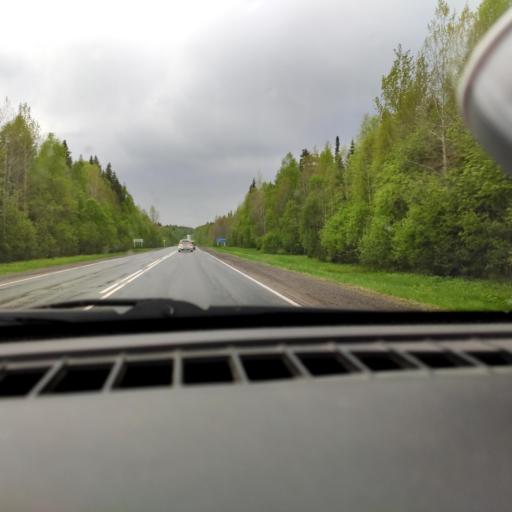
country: RU
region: Perm
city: Perm
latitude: 58.1584
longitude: 56.2481
